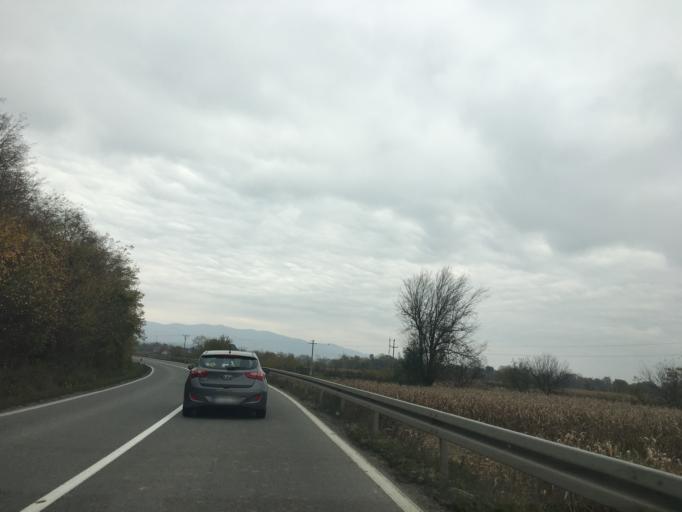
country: RS
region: Central Serbia
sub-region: Raski Okrug
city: Kraljevo
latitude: 43.7114
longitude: 20.7882
